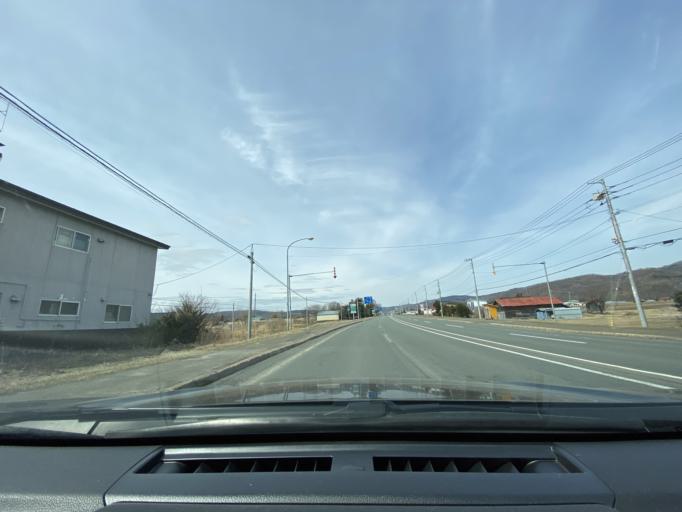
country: JP
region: Hokkaido
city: Kitami
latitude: 43.7952
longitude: 143.7443
